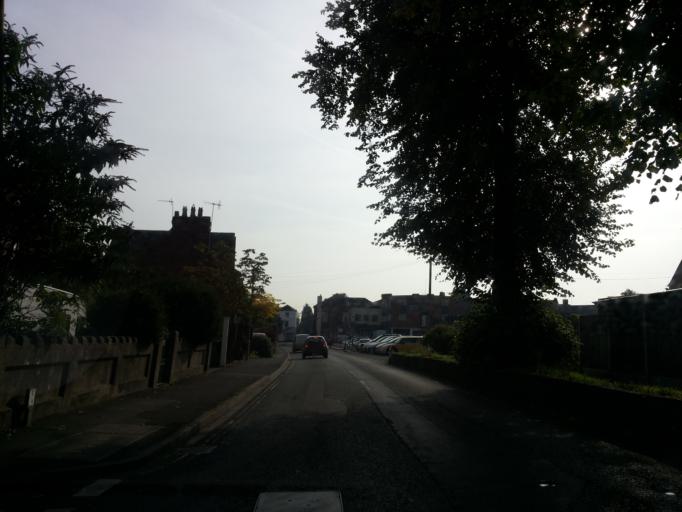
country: GB
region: England
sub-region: Worcestershire
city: Stourport-on-Severn
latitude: 52.3413
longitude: -2.2806
